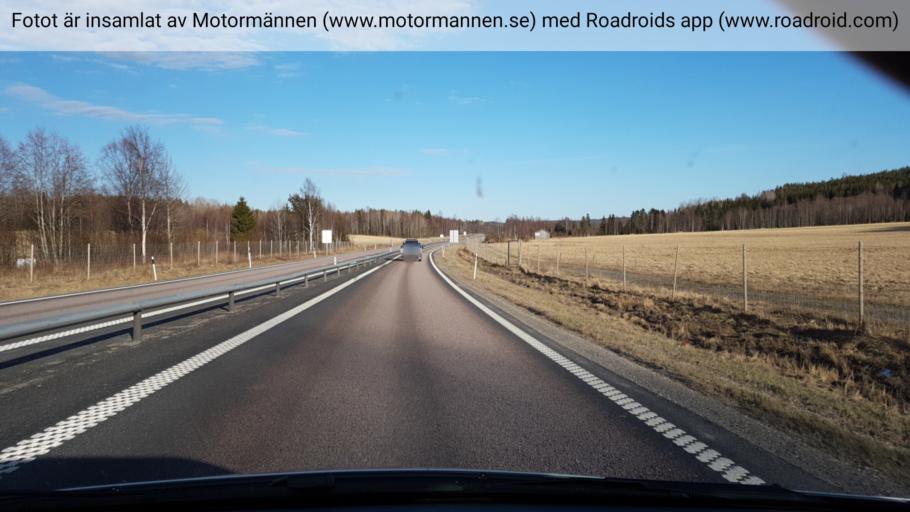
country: SE
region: Vaesternorrland
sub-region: OErnskoeldsviks Kommun
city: Ornskoldsvik
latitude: 63.3093
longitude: 18.8402
